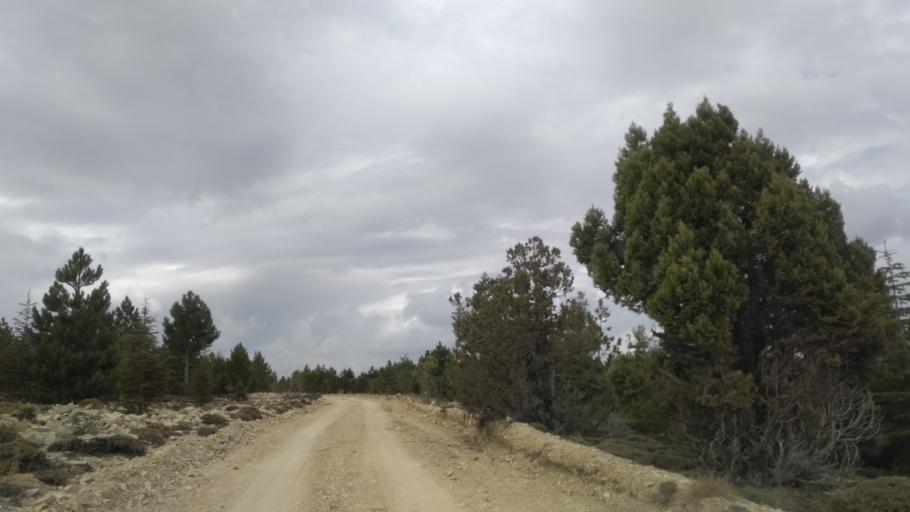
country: TR
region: Mersin
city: Sarikavak
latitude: 36.5714
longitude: 33.7552
